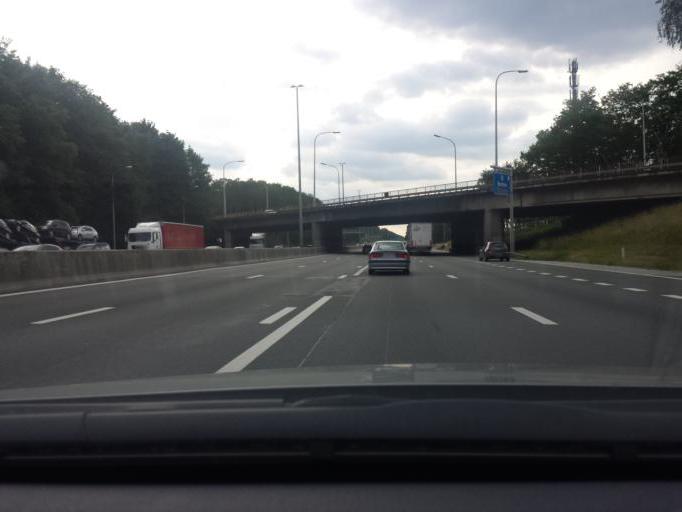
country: BE
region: Flanders
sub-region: Provincie Vlaams-Brabant
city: Bertem
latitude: 50.8608
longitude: 4.6139
